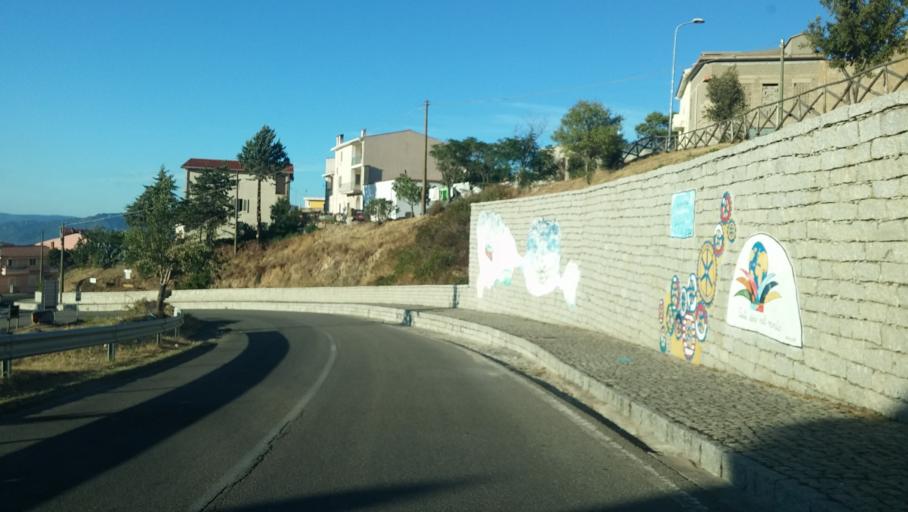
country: IT
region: Sardinia
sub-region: Provincia di Nuoro
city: Orgosolo
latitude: 40.2047
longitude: 9.3485
